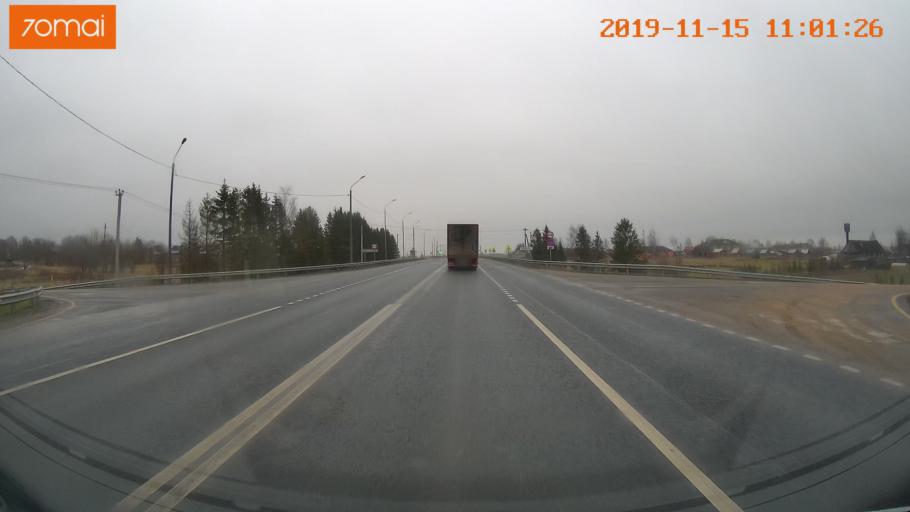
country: RU
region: Vologda
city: Chebsara
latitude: 59.1328
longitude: 38.9210
